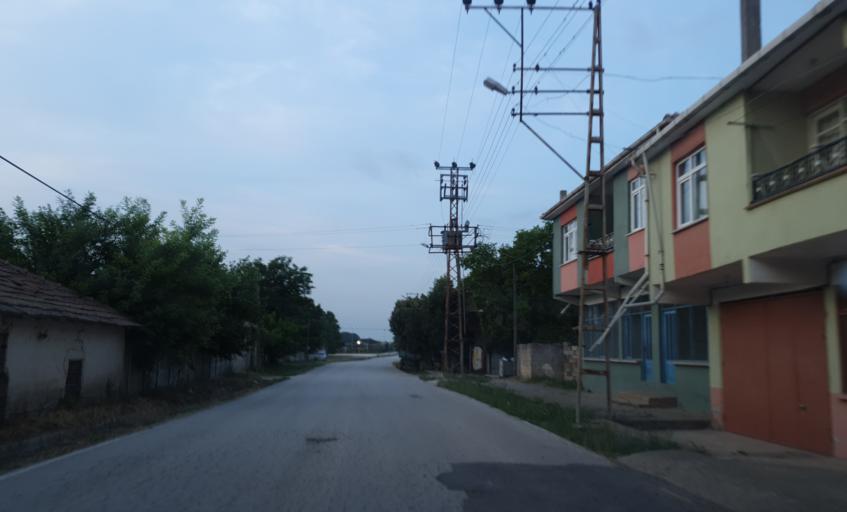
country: TR
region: Tekirdag
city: Beyazkoy
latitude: 41.3867
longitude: 27.6219
